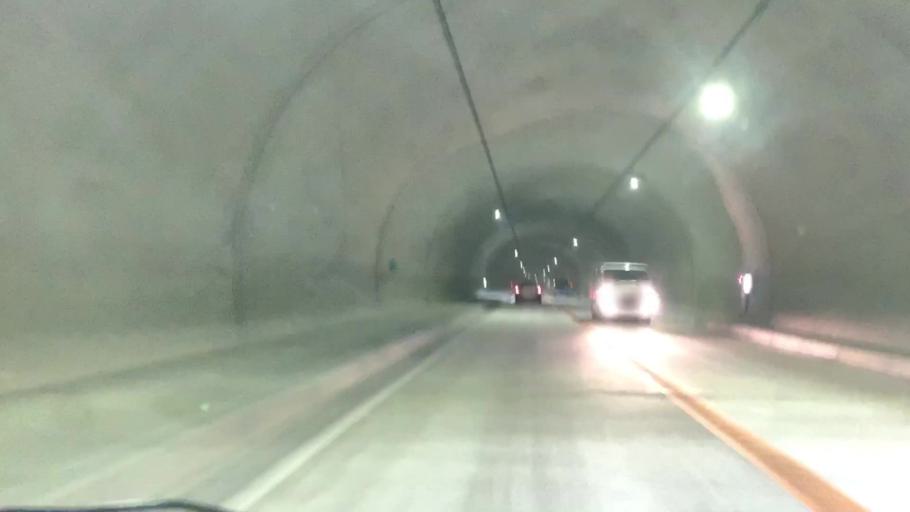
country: JP
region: Saga Prefecture
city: Takeocho-takeo
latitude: 33.2603
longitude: 130.0281
